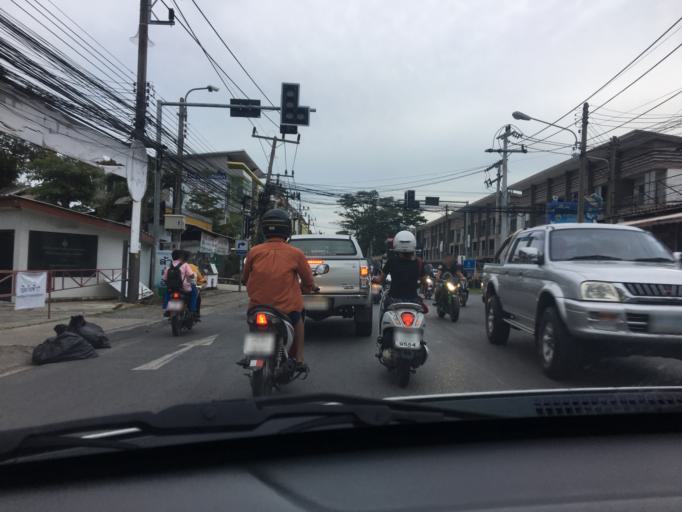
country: TH
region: Phuket
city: Ban Ratsada
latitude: 7.9074
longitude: 98.4030
